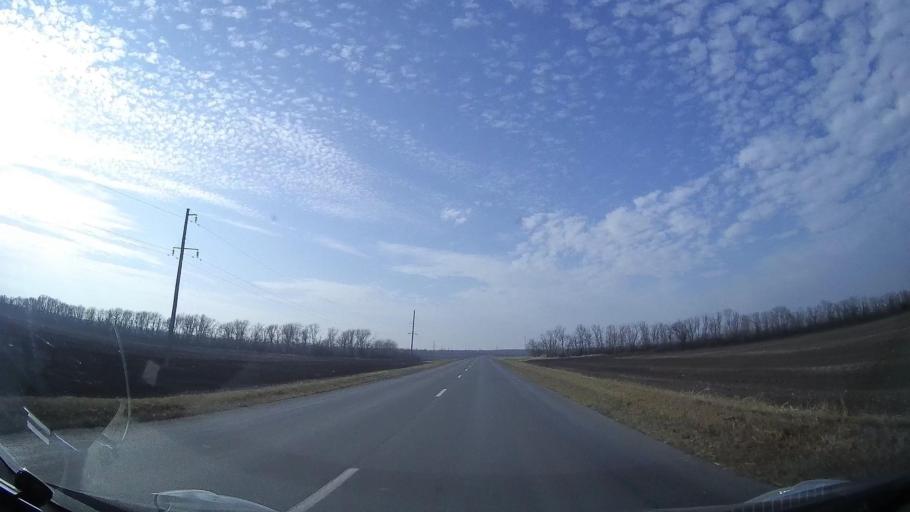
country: RU
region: Rostov
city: Veselyy
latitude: 46.9691
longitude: 40.6446
